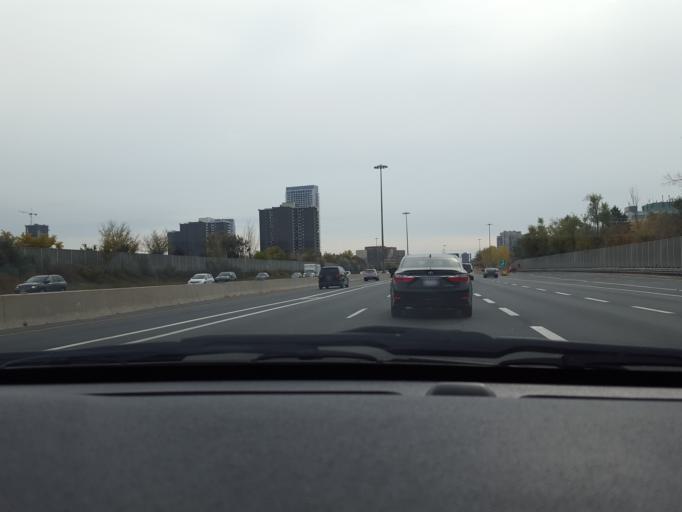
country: CA
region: Ontario
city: Willowdale
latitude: 43.7830
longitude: -79.3412
